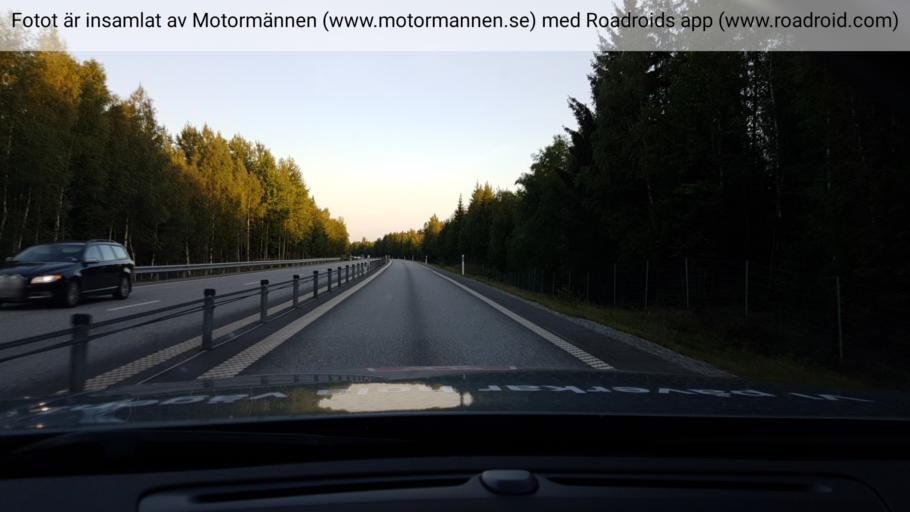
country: SE
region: Vaestmanland
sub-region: Surahammars Kommun
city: Surahammar
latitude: 59.7347
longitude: 16.2290
